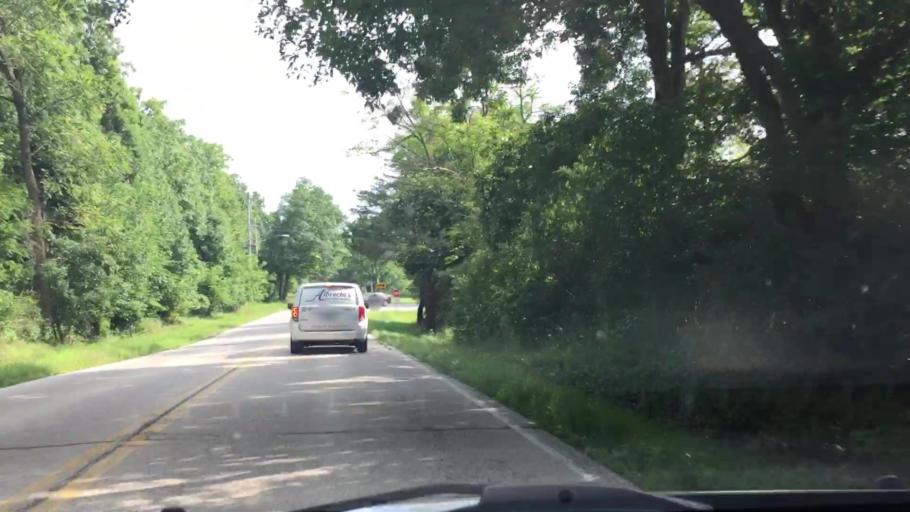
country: US
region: Wisconsin
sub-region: Waukesha County
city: Wales
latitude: 43.0415
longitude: -88.3496
